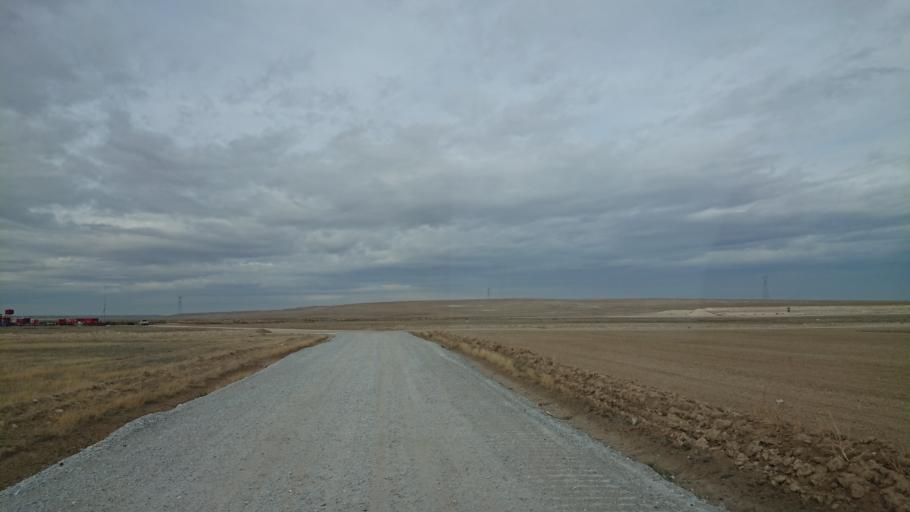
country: TR
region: Aksaray
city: Sultanhani
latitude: 38.1334
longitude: 33.5517
